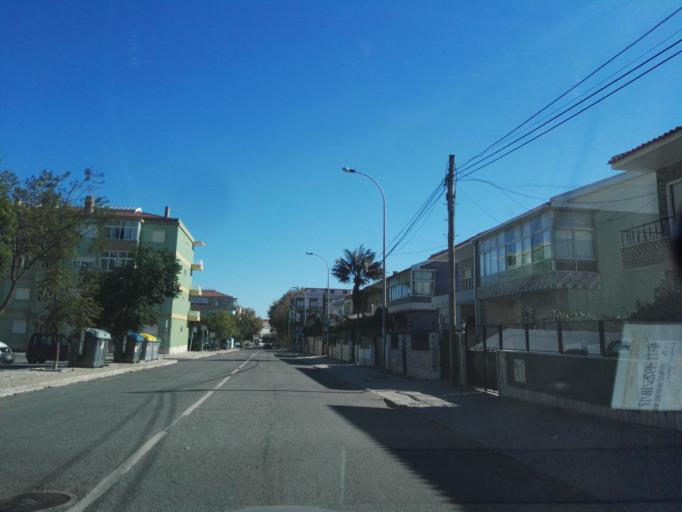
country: PT
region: Lisbon
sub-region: Sintra
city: Sintra
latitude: 38.7977
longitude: -9.3507
